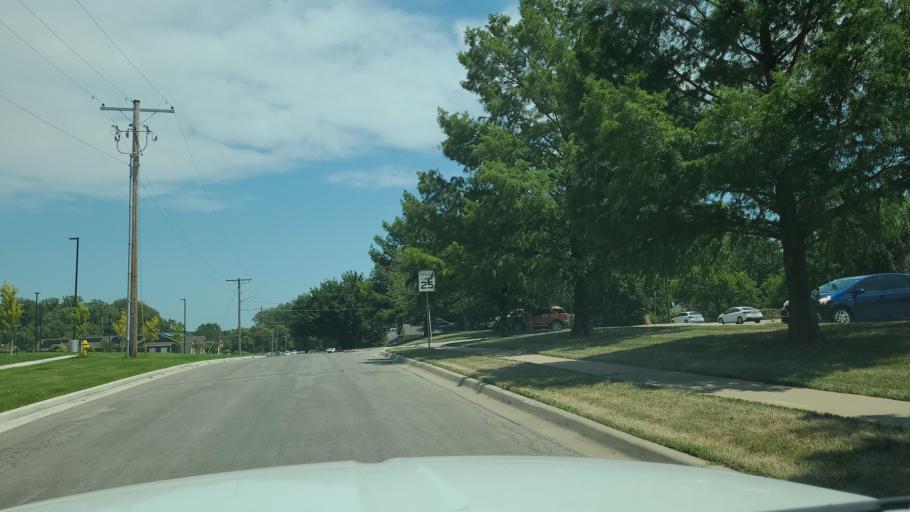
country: US
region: Kansas
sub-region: Douglas County
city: Lawrence
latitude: 38.9808
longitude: -95.2474
